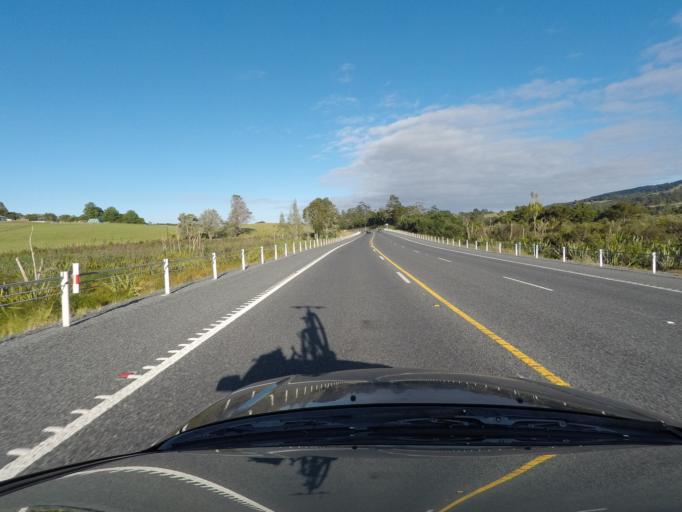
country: NZ
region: Northland
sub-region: Far North District
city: Kawakawa
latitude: -35.4975
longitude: 174.1632
